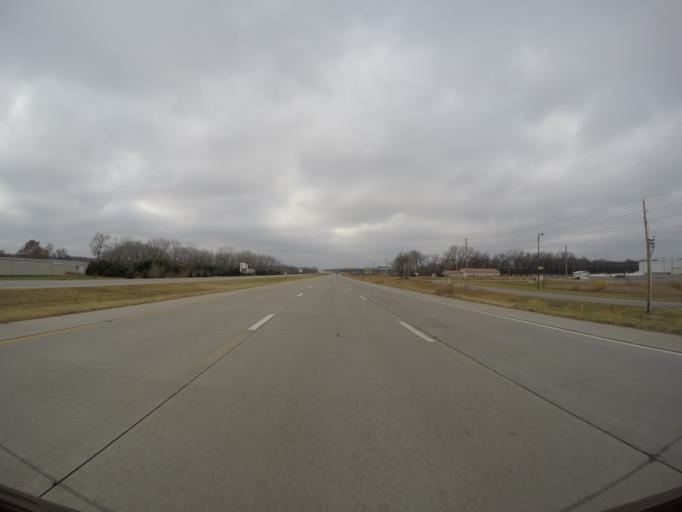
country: US
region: Kansas
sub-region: Geary County
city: Junction City
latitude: 38.9998
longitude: -96.8664
